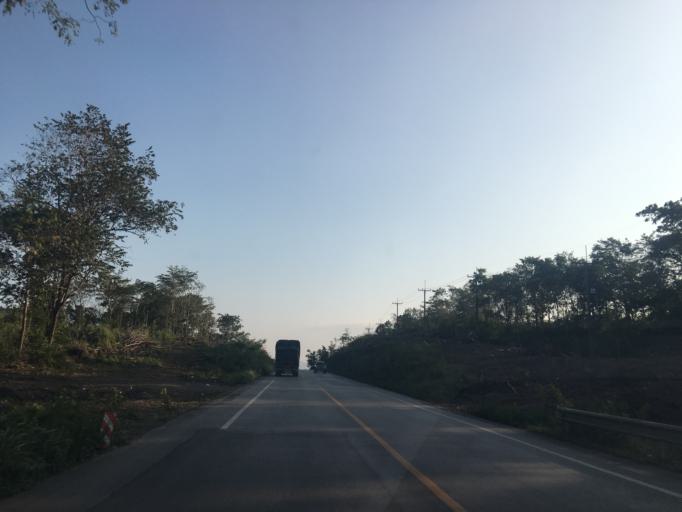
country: TH
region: Lampang
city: Ngao
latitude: 18.6520
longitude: 100.0177
